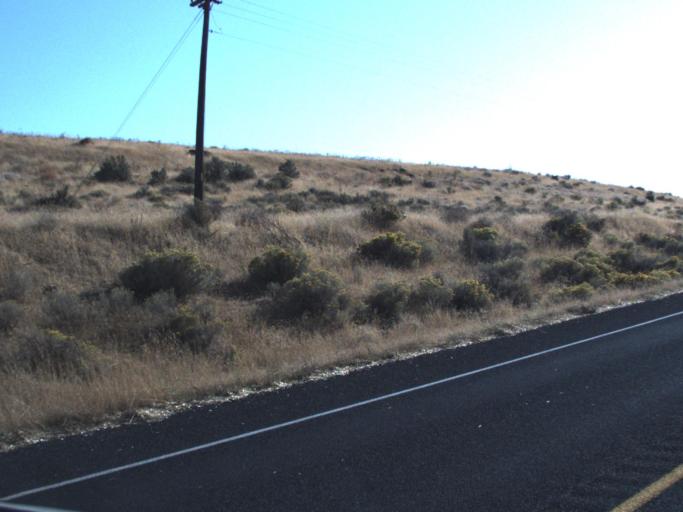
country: US
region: Oregon
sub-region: Morrow County
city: Boardman
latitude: 45.8927
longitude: -119.6959
